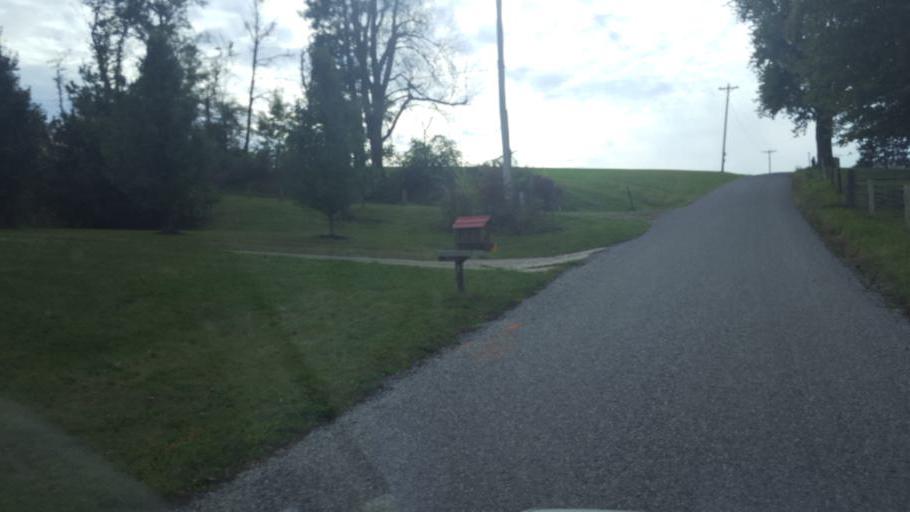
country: US
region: Ohio
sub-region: Holmes County
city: Millersburg
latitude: 40.5855
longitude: -81.8392
